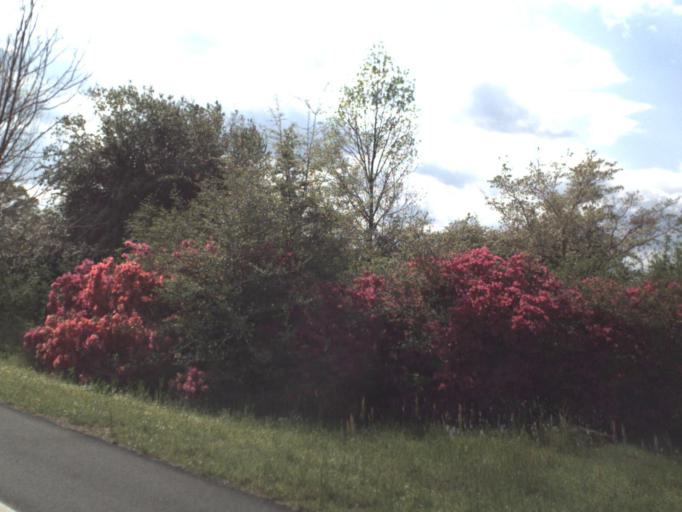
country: US
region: Florida
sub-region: Okaloosa County
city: Crestview
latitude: 30.8961
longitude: -86.5045
